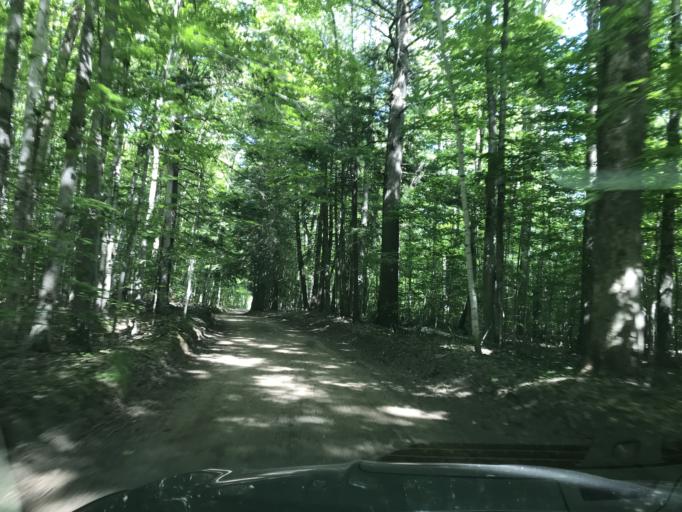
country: US
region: Michigan
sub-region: Cheboygan County
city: Indian River
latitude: 45.5928
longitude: -84.6821
